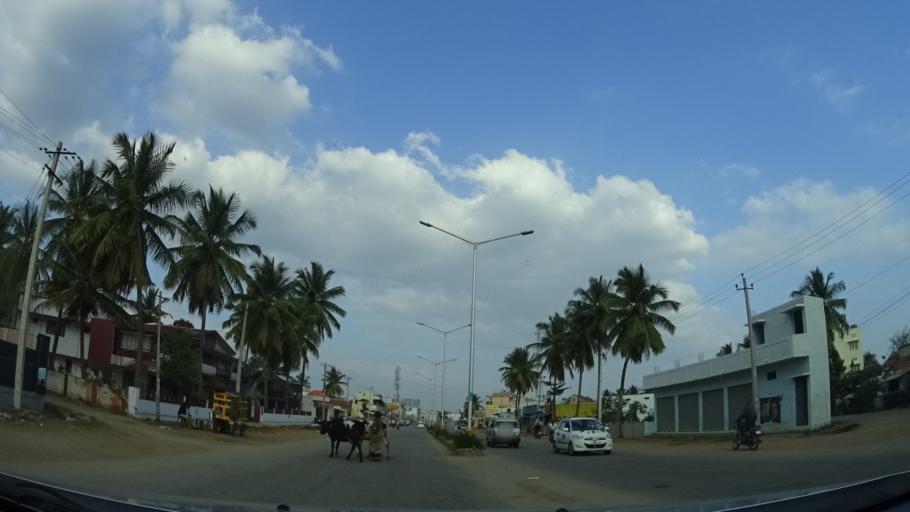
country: IN
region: Karnataka
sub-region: Mandya
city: Malavalli
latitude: 12.3833
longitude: 77.0506
